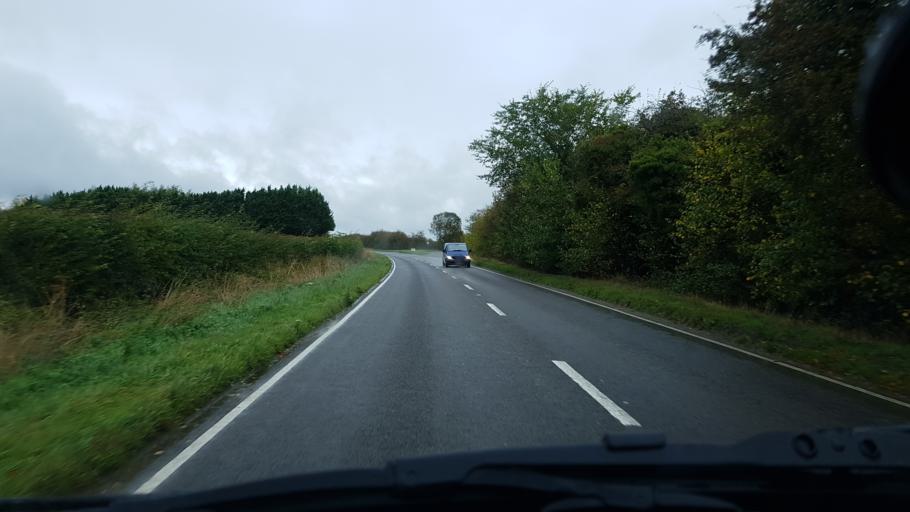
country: GB
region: England
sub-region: Oxfordshire
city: Ducklington
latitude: 51.7331
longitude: -1.4434
